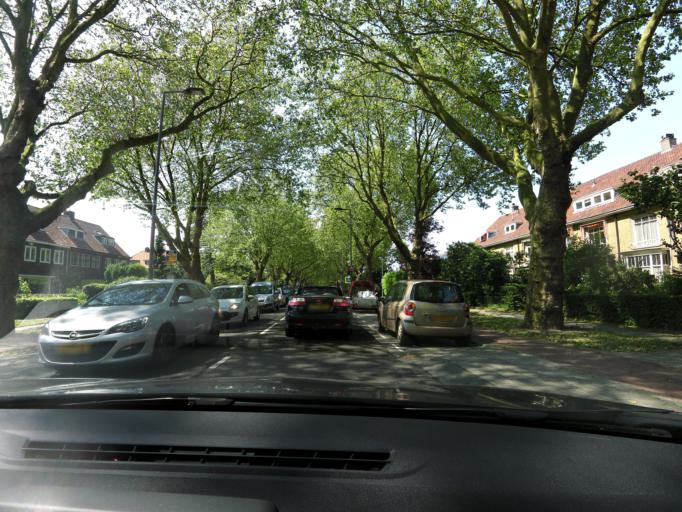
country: NL
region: South Holland
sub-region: Gemeente Lansingerland
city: Bergschenhoek
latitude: 51.9570
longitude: 4.5090
